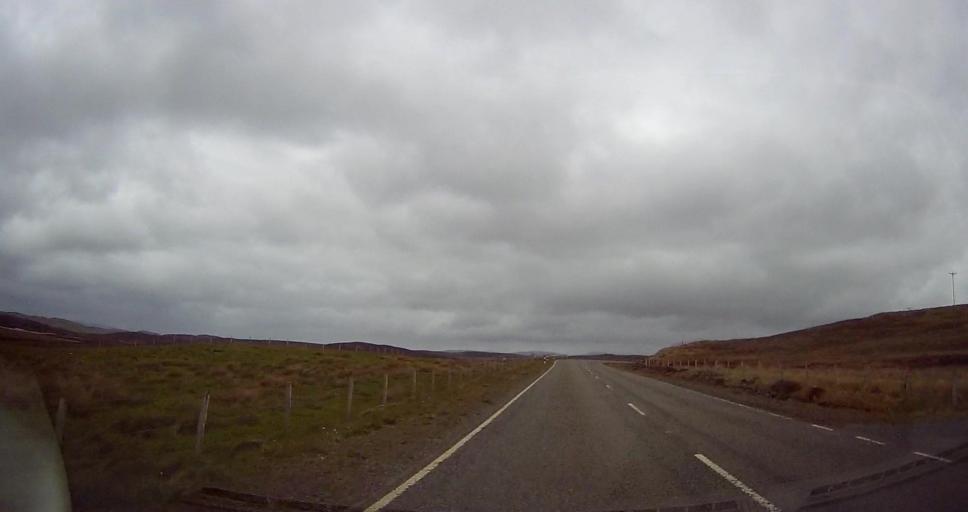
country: GB
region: Scotland
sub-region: Shetland Islands
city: Sandwick
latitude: 60.2585
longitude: -1.4938
